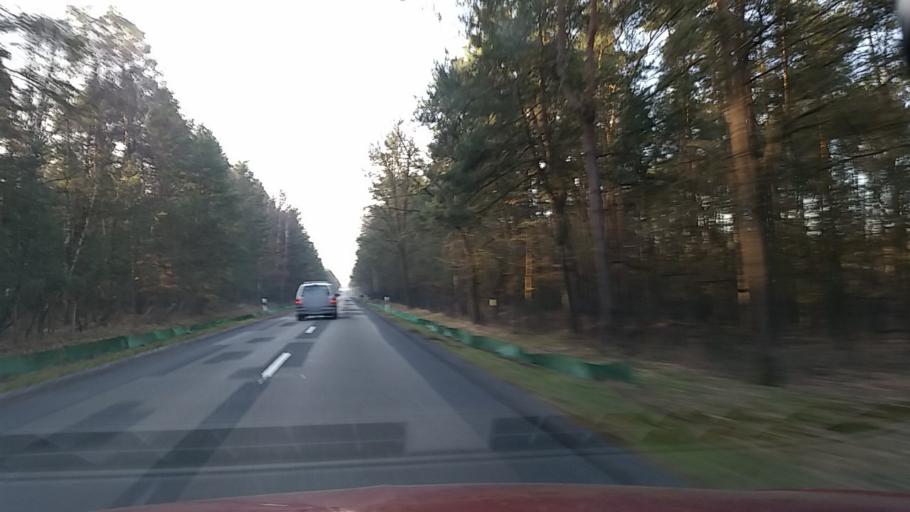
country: DE
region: Lower Saxony
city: Schoneworde
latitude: 52.5762
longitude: 10.6786
